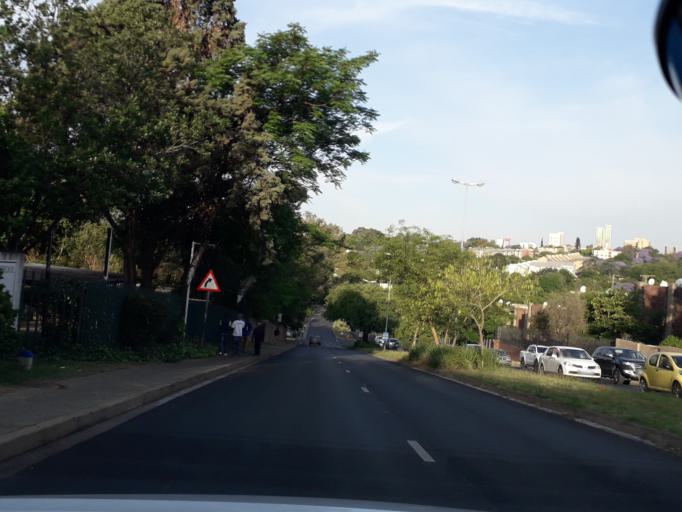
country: ZA
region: Gauteng
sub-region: City of Johannesburg Metropolitan Municipality
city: Johannesburg
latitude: -26.0919
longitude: 27.9880
